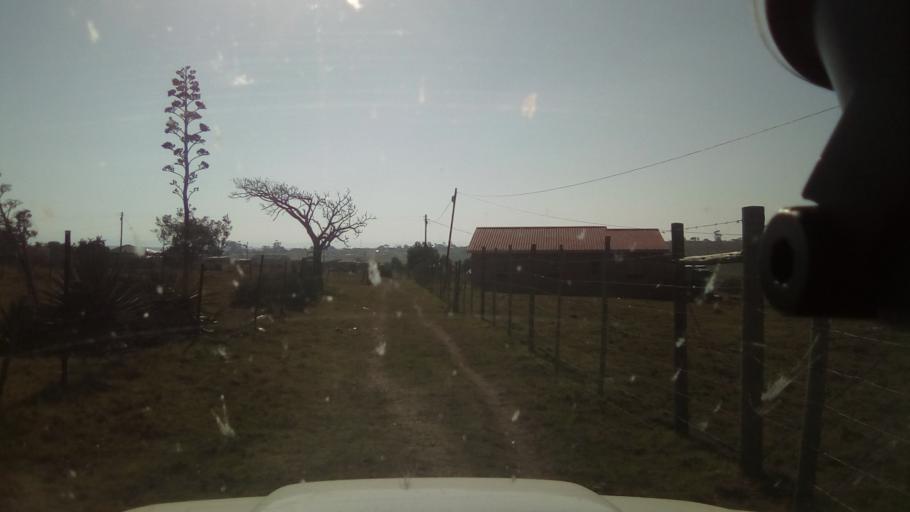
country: ZA
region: Eastern Cape
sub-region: Buffalo City Metropolitan Municipality
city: Bhisho
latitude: -32.9504
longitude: 27.3238
